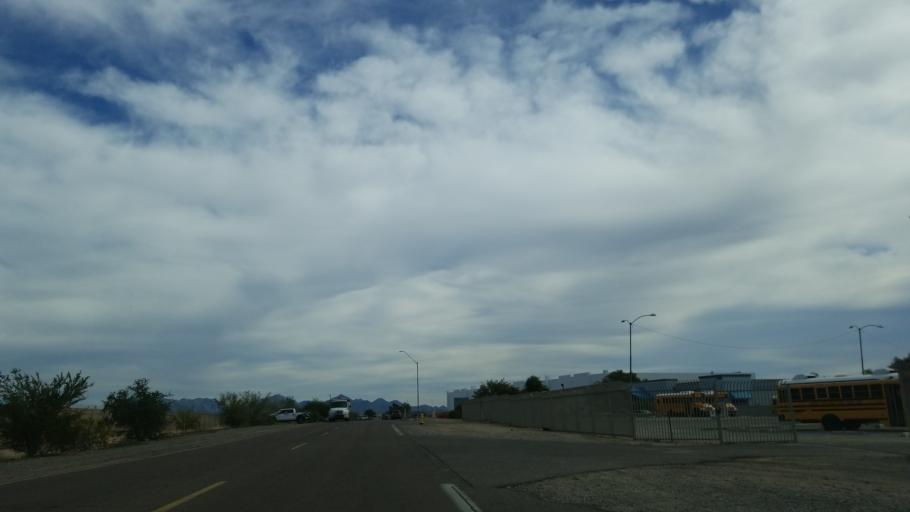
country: US
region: Arizona
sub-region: Maricopa County
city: Paradise Valley
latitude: 33.6762
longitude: -112.0167
